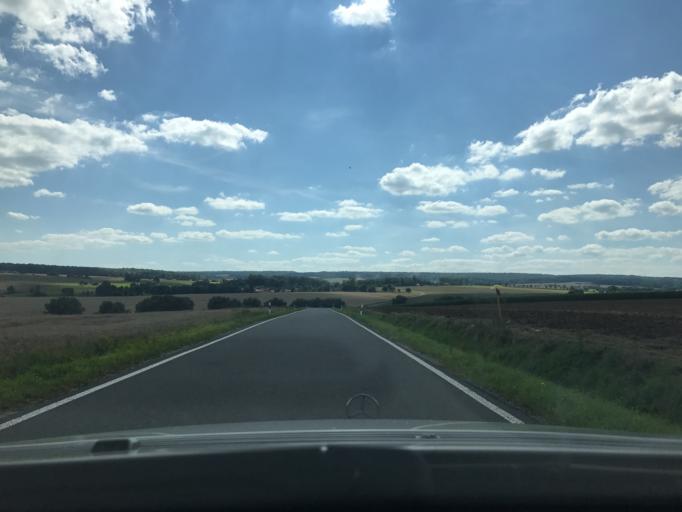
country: DE
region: Thuringia
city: Anrode
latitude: 51.2483
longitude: 10.3816
